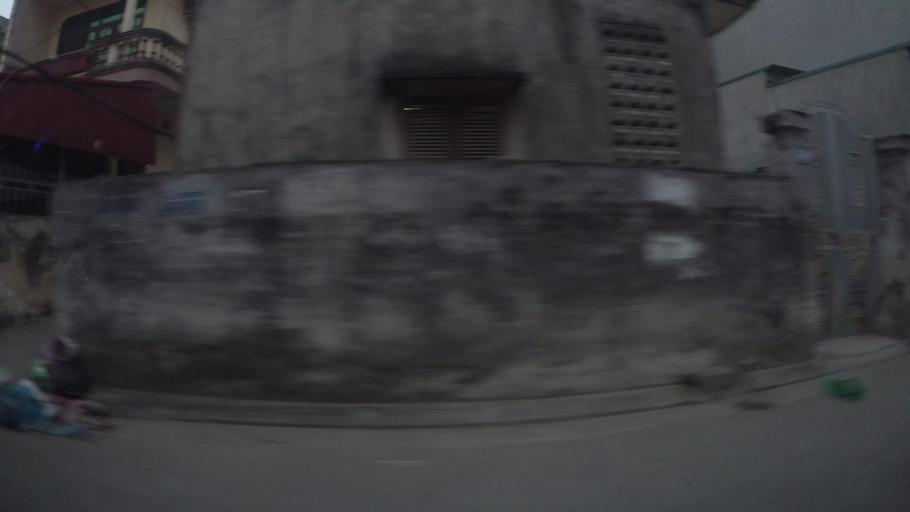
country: VN
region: Ha Noi
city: Trau Quy
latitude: 21.0432
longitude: 105.8979
